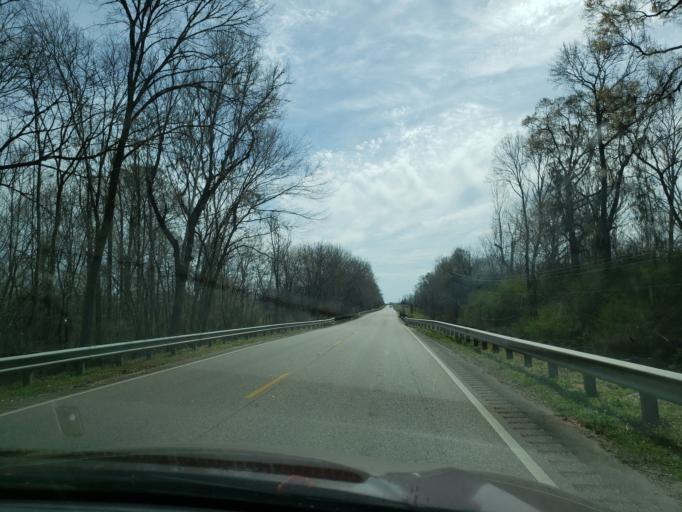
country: US
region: Alabama
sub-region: Dallas County
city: Selma
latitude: 32.4502
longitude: -87.0774
